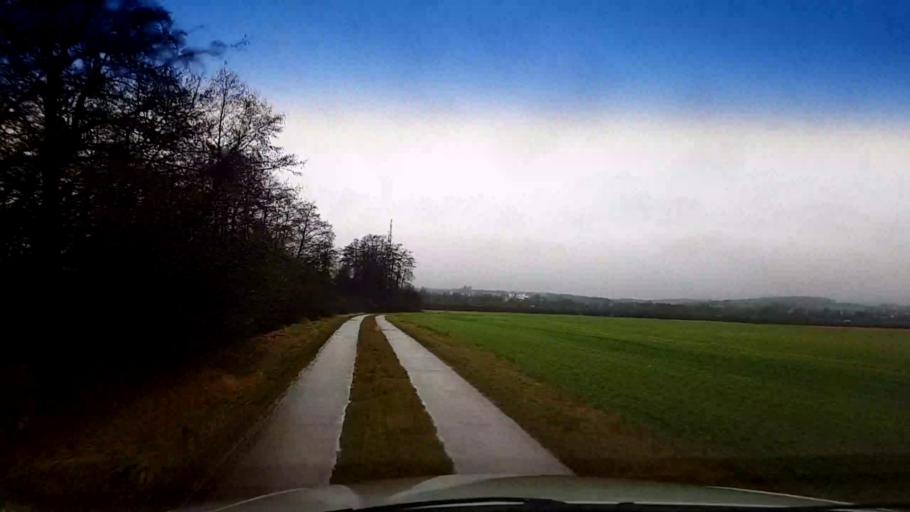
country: DE
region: Bavaria
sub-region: Upper Franconia
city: Bischberg
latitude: 49.9248
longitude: 10.8392
